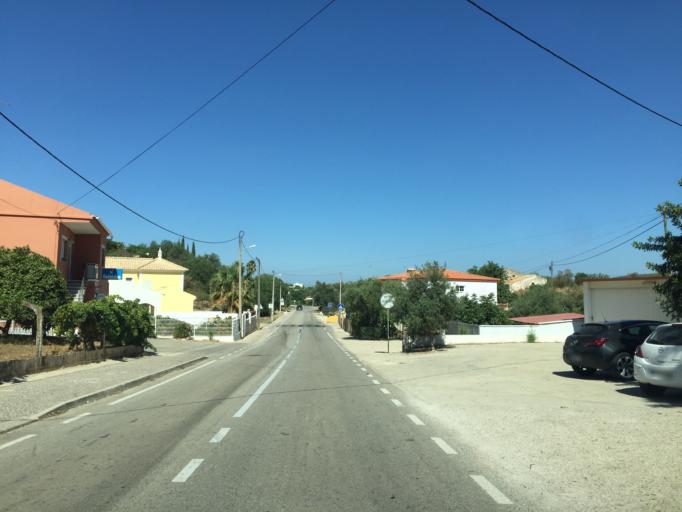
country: PT
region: Faro
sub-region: Loule
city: Vilamoura
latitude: 37.1185
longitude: -8.0951
